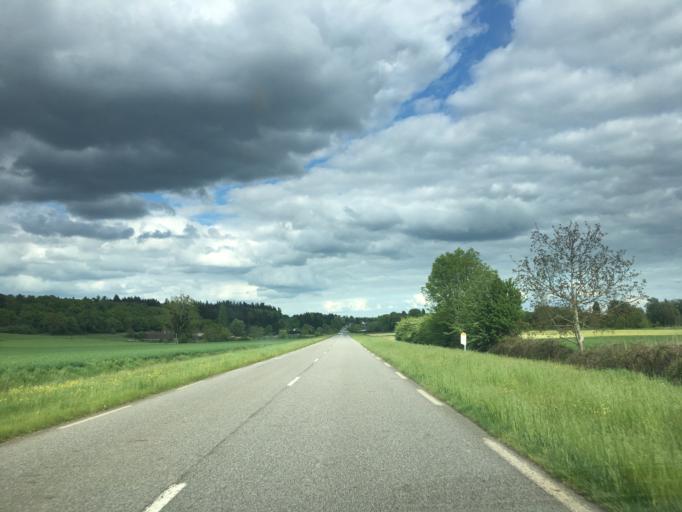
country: FR
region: Haute-Normandie
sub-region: Departement de l'Eure
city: Nonancourt
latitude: 48.7724
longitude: 1.1711
